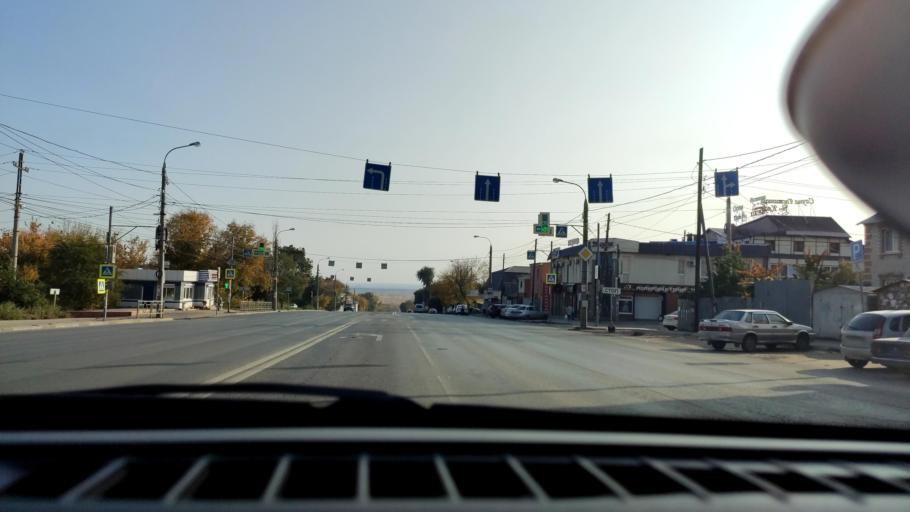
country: RU
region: Samara
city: Samara
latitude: 53.1855
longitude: 50.1914
